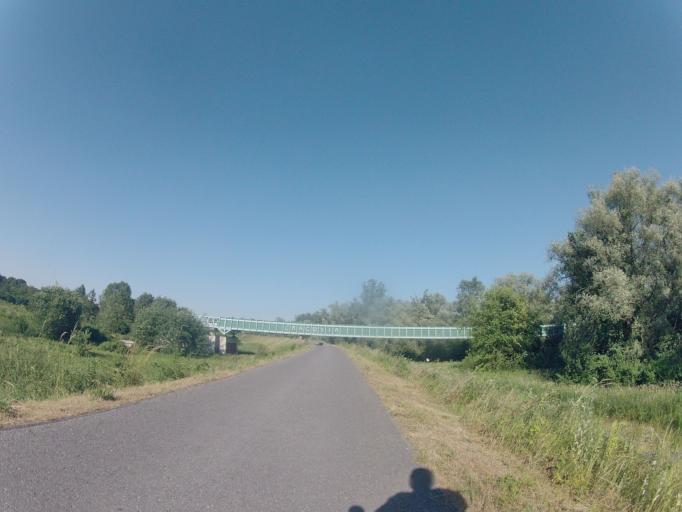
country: PL
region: Lesser Poland Voivodeship
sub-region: Krakow
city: Krakow
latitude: 50.0400
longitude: 19.8918
